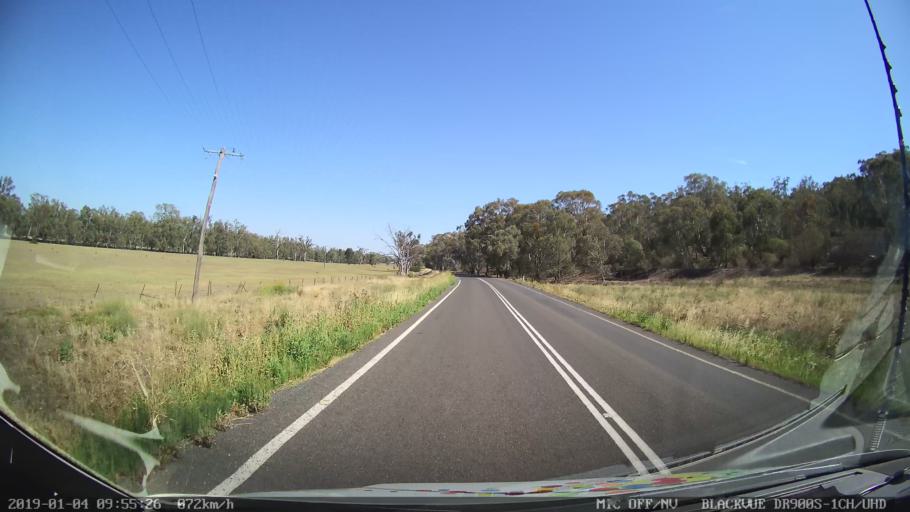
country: AU
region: New South Wales
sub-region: Cabonne
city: Canowindra
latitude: -33.5350
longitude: 148.4040
